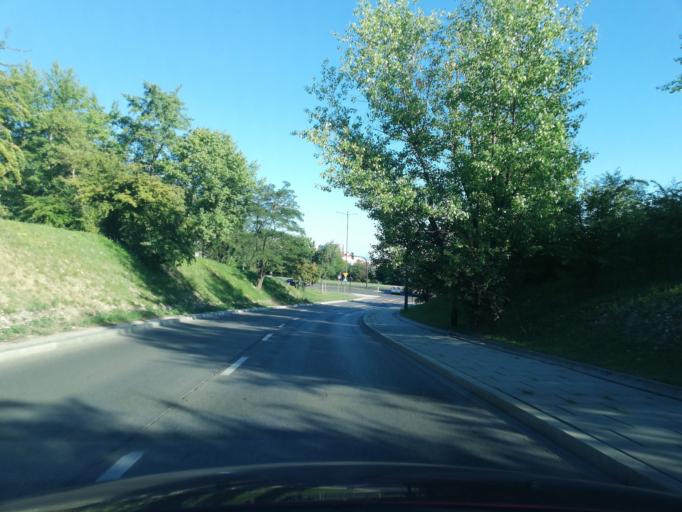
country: PL
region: Lesser Poland Voivodeship
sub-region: Krakow
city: Krakow
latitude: 50.0879
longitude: 19.9910
